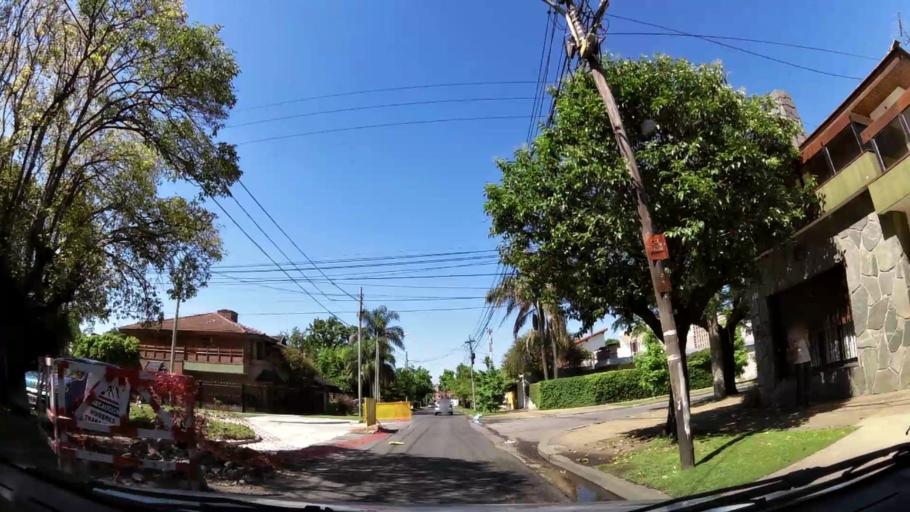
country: AR
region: Buenos Aires
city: Ituzaingo
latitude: -34.6463
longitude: -58.6640
